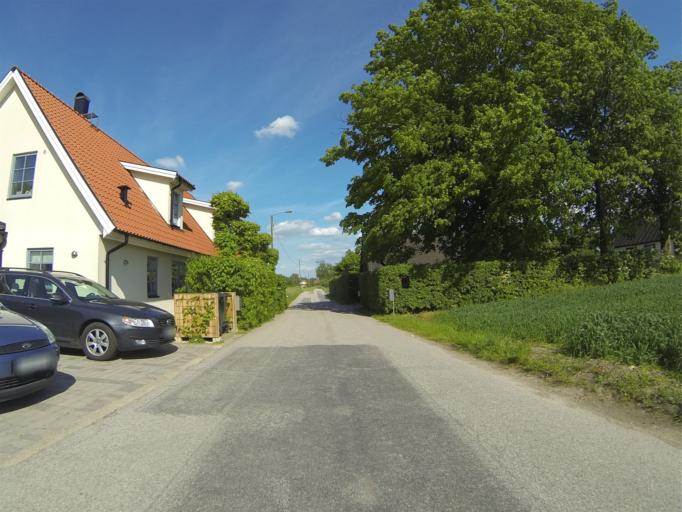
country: SE
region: Skane
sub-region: Lunds Kommun
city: Lund
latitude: 55.6859
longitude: 13.2294
